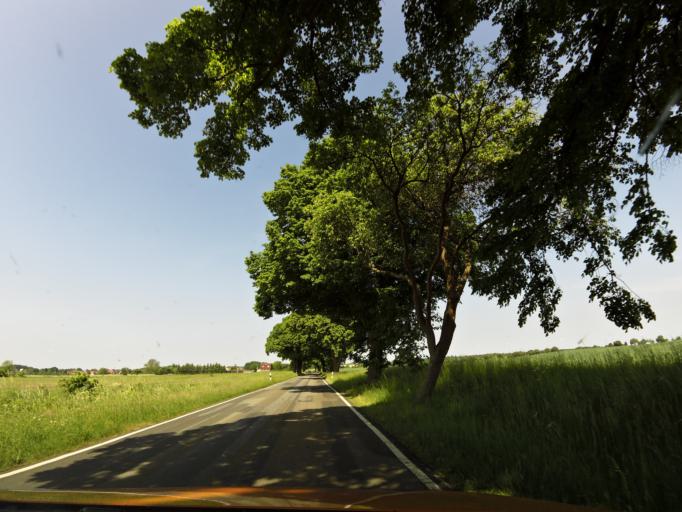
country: DE
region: Mecklenburg-Vorpommern
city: Parchim
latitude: 53.4188
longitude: 11.8775
